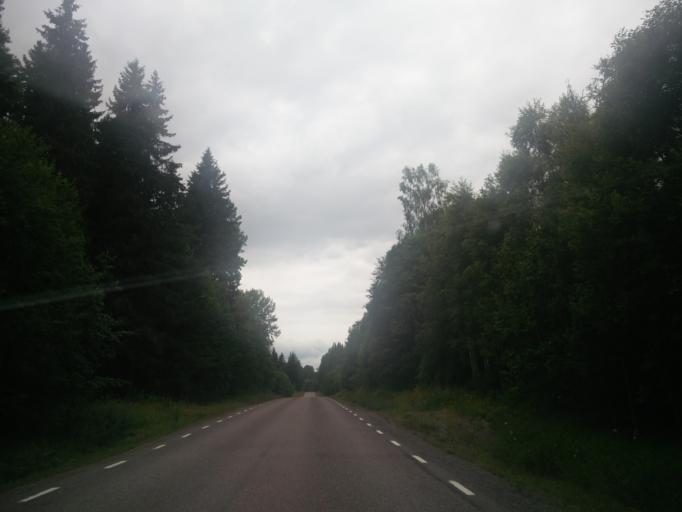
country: SE
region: Vaermland
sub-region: Arvika Kommun
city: Arvika
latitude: 59.9529
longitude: 12.7300
